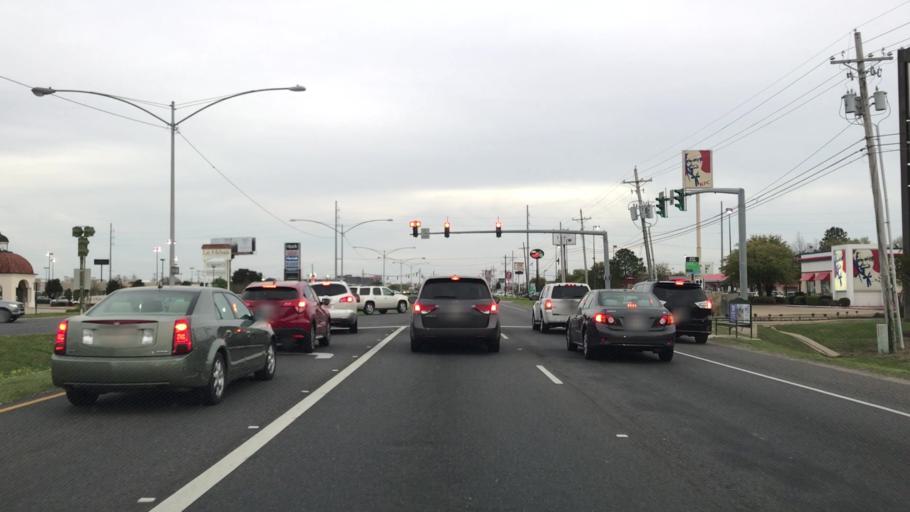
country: US
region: Louisiana
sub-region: Bossier Parish
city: Bossier City
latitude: 32.4460
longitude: -93.7202
